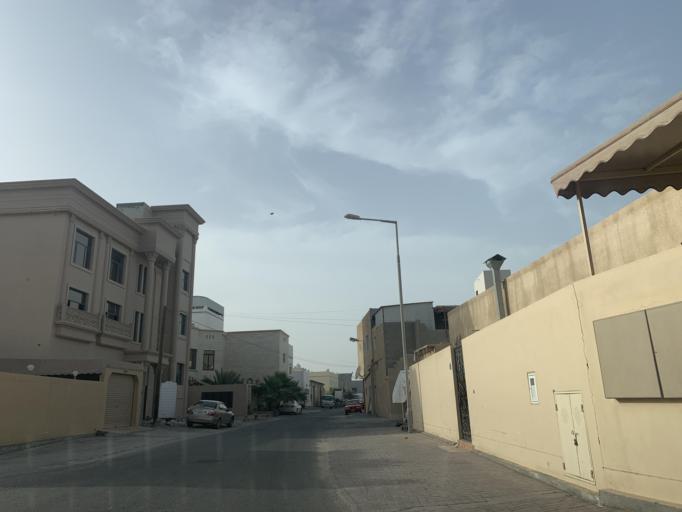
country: BH
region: Northern
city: Madinat `Isa
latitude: 26.1603
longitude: 50.5122
